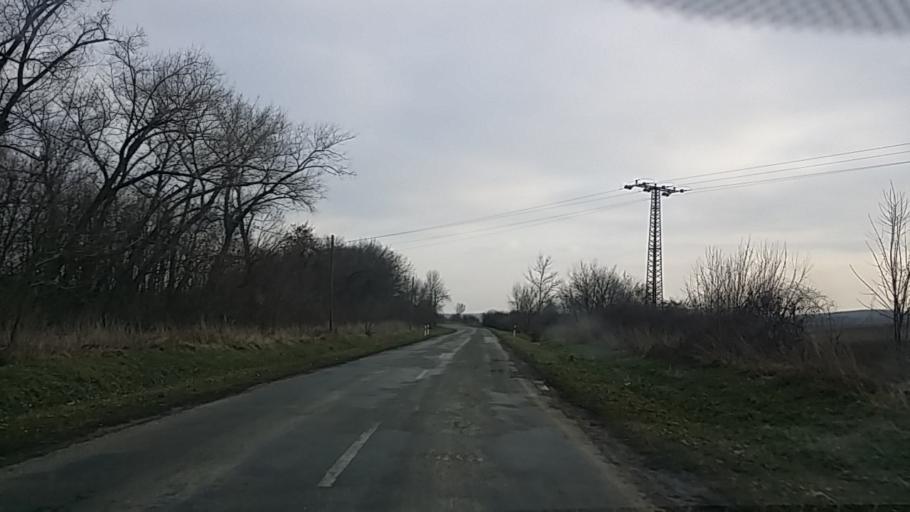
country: HU
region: Baranya
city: Lanycsok
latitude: 46.1023
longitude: 18.5442
